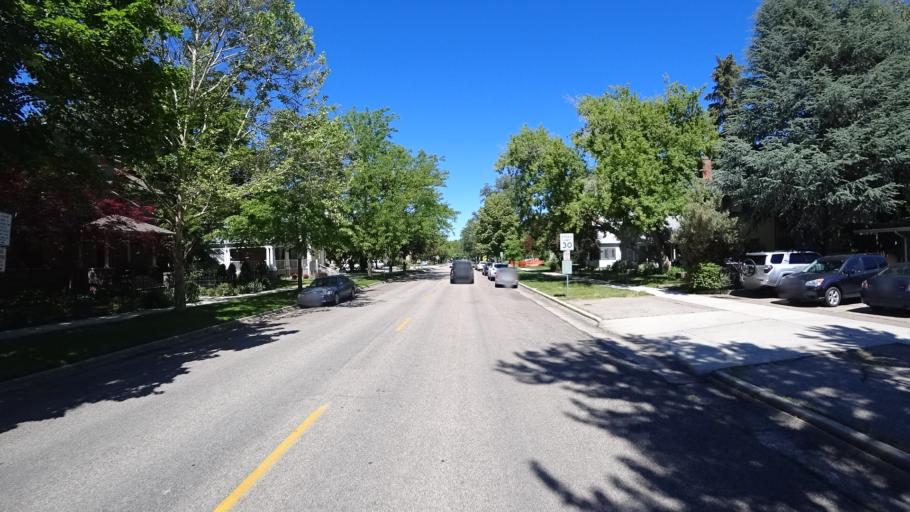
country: US
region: Idaho
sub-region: Ada County
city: Boise
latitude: 43.6222
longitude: -116.2008
